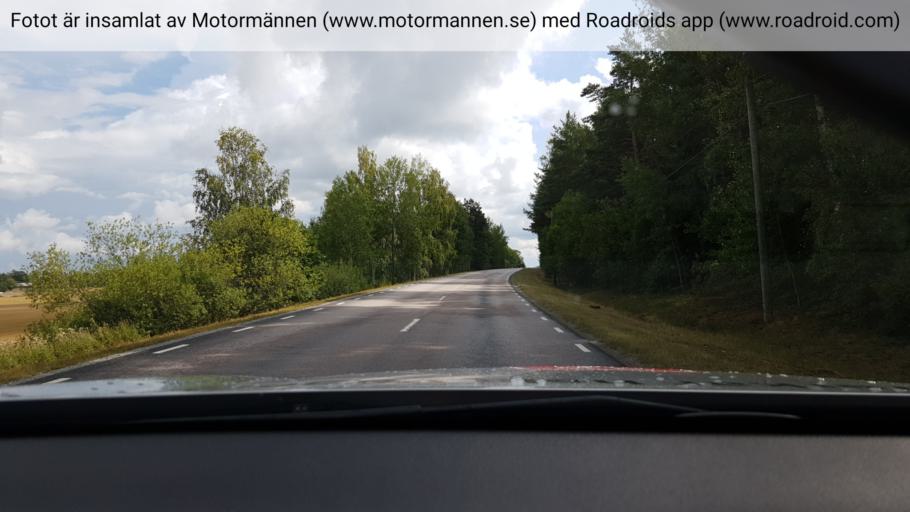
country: SE
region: Stockholm
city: Stenhamra
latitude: 59.3697
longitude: 17.6080
